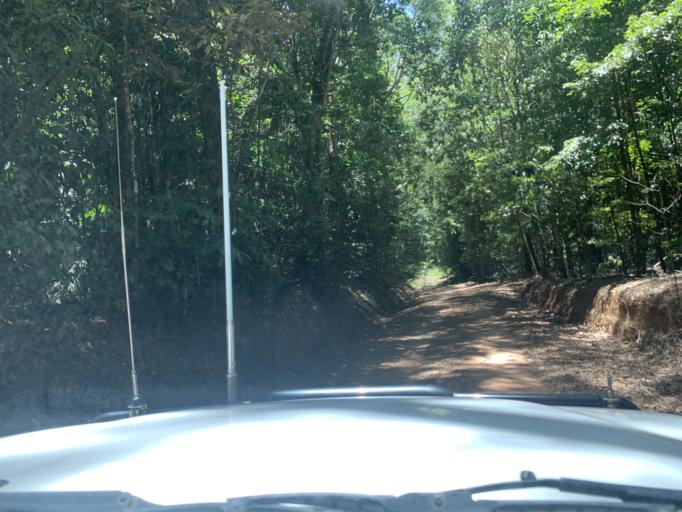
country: AU
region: Queensland
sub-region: Cairns
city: Redlynch
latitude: -16.9441
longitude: 145.6301
